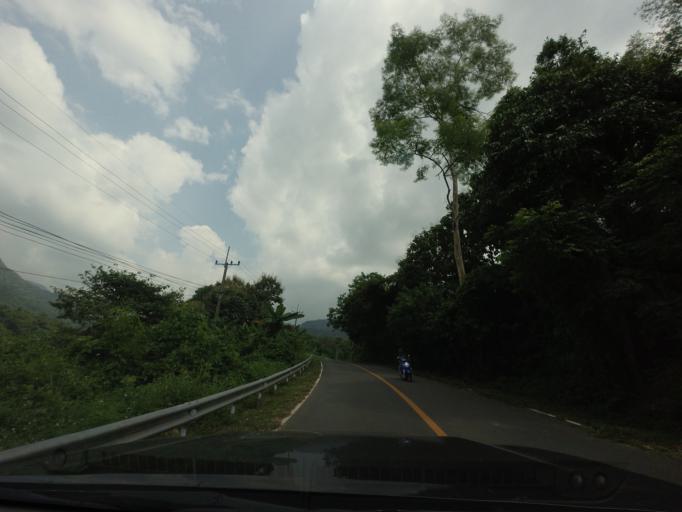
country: TH
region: Nan
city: Pua
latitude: 19.1800
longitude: 100.9609
